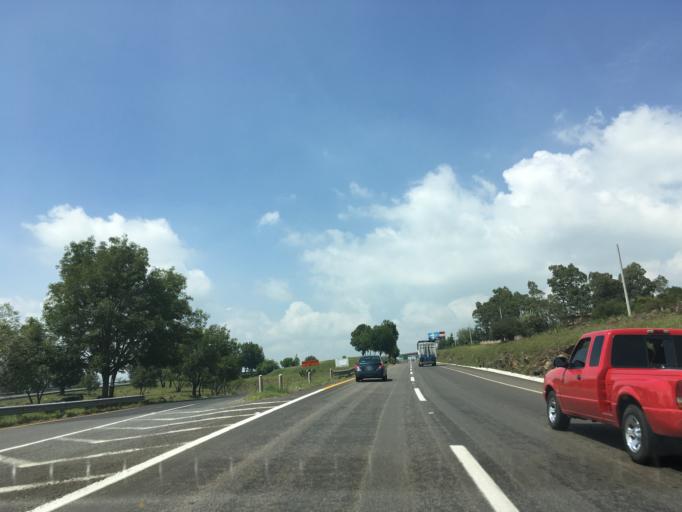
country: MX
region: Michoacan
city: Acuitzio del Canje
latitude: 19.5568
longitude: -101.3348
